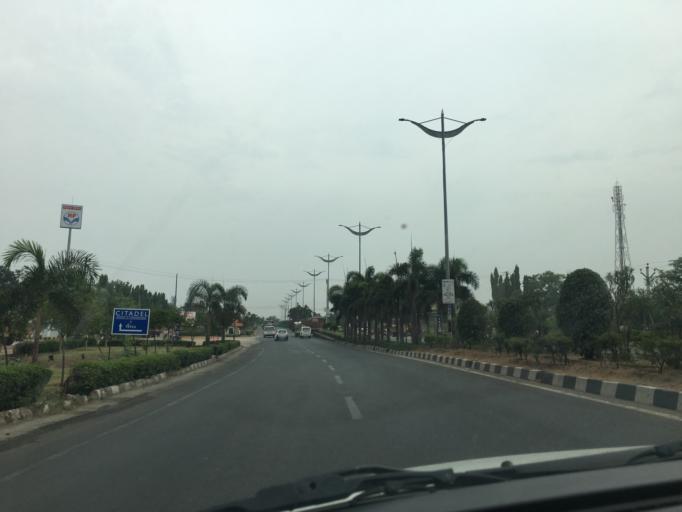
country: IN
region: Telangana
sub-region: Rangareddi
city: Balapur
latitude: 17.2948
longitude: 78.4178
